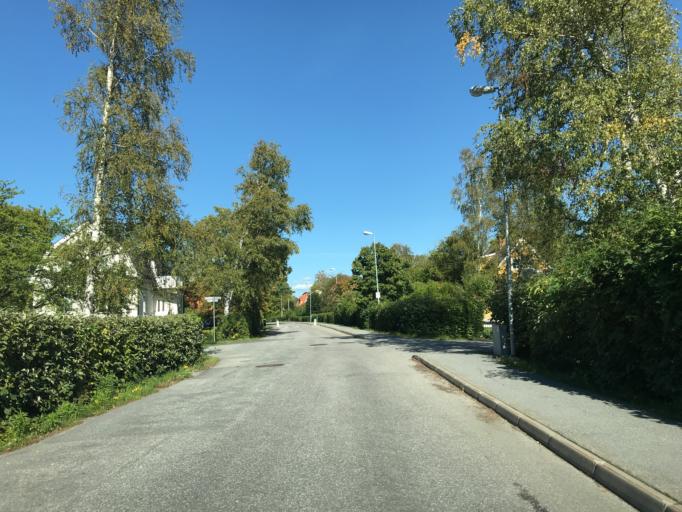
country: SE
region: Stockholm
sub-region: Sollentuna Kommun
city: Sollentuna
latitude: 59.4175
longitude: 17.9645
